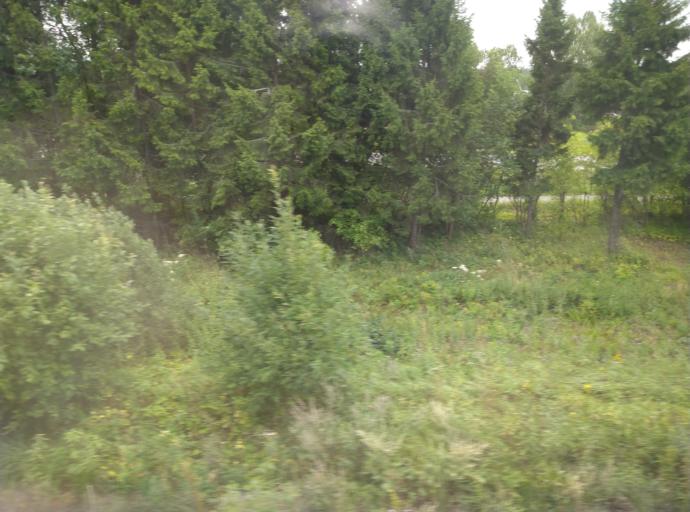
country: RU
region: Jaroslavl
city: Burmakino
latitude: 57.4371
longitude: 40.3064
